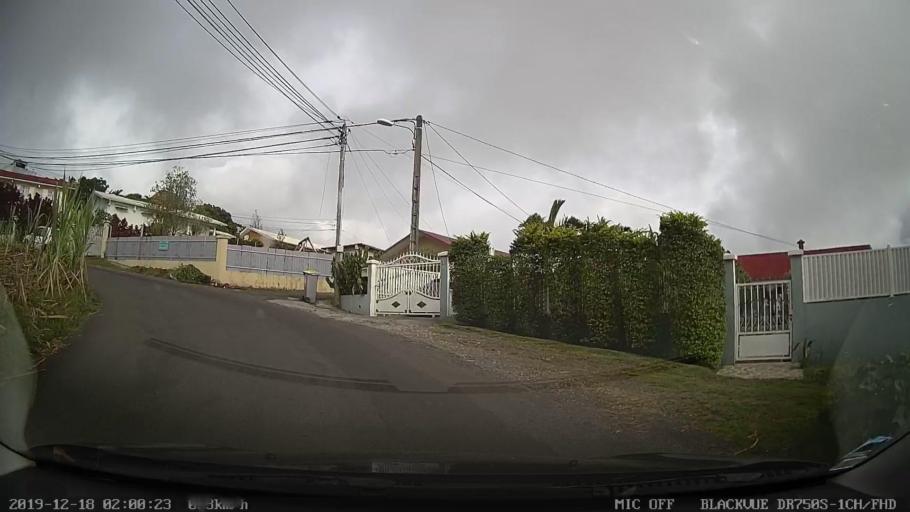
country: RE
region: Reunion
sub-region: Reunion
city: Le Tampon
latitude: -21.2535
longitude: 55.5178
